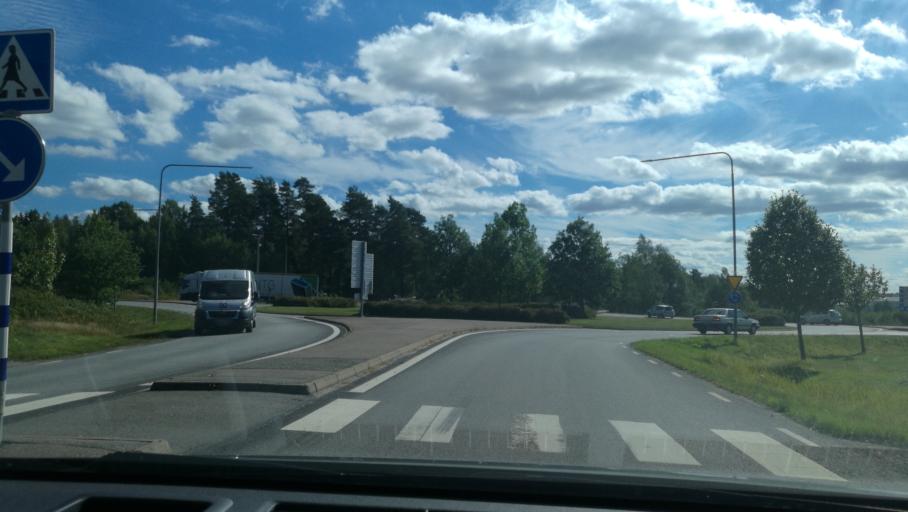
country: SE
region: Vaestra Goetaland
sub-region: Mariestads Kommun
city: Mariestad
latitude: 58.6929
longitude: 13.8409
